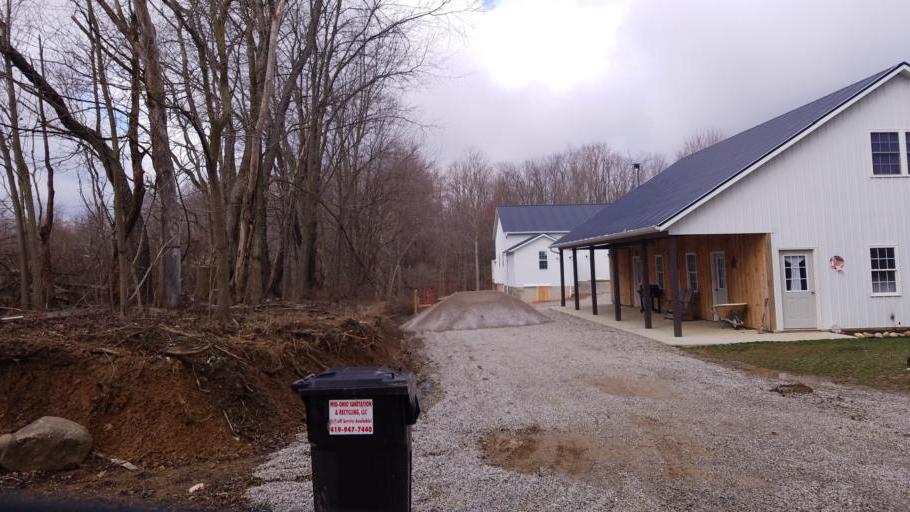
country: US
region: Ohio
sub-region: Morrow County
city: Mount Gilead
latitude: 40.5579
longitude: -82.7007
